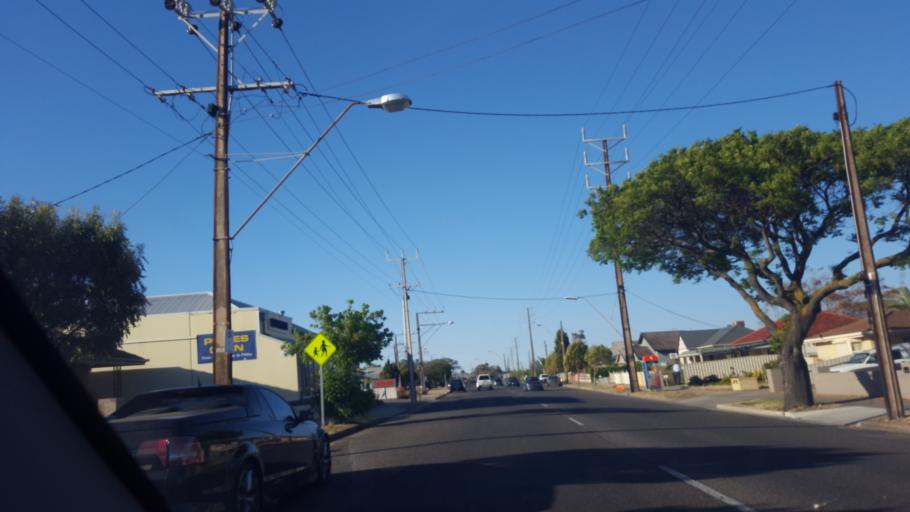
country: AU
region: South Australia
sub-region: Port Adelaide Enfield
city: Birkenhead
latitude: -34.8175
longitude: 138.4938
